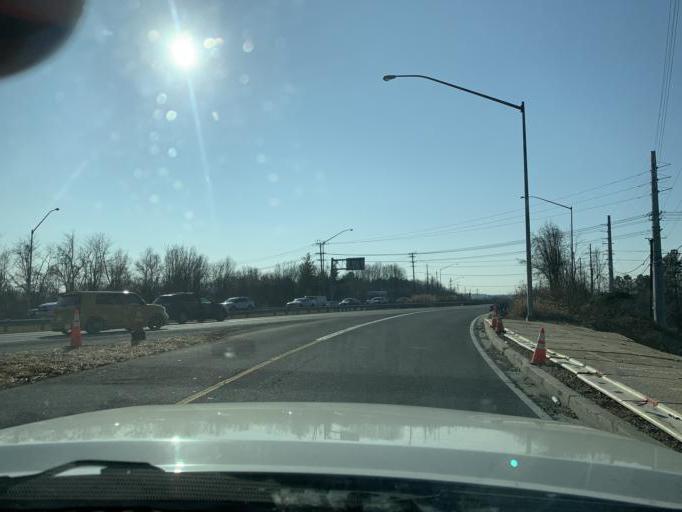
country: US
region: Maryland
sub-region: Prince George's County
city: Largo
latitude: 38.8991
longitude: -76.8304
